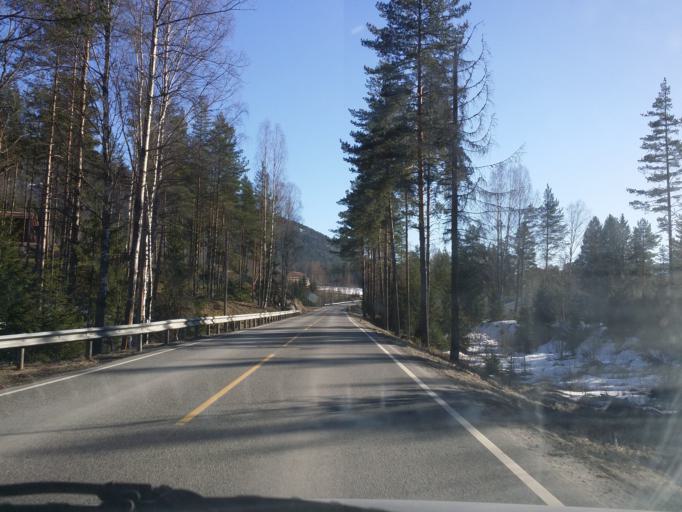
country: NO
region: Buskerud
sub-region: Ringerike
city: Honefoss
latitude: 60.3527
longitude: 10.1004
